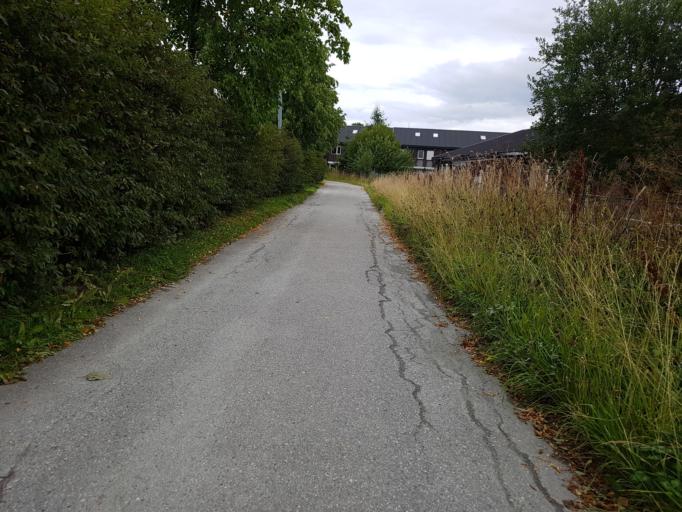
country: NO
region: Sor-Trondelag
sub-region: Trondheim
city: Trondheim
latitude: 63.4126
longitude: 10.4683
